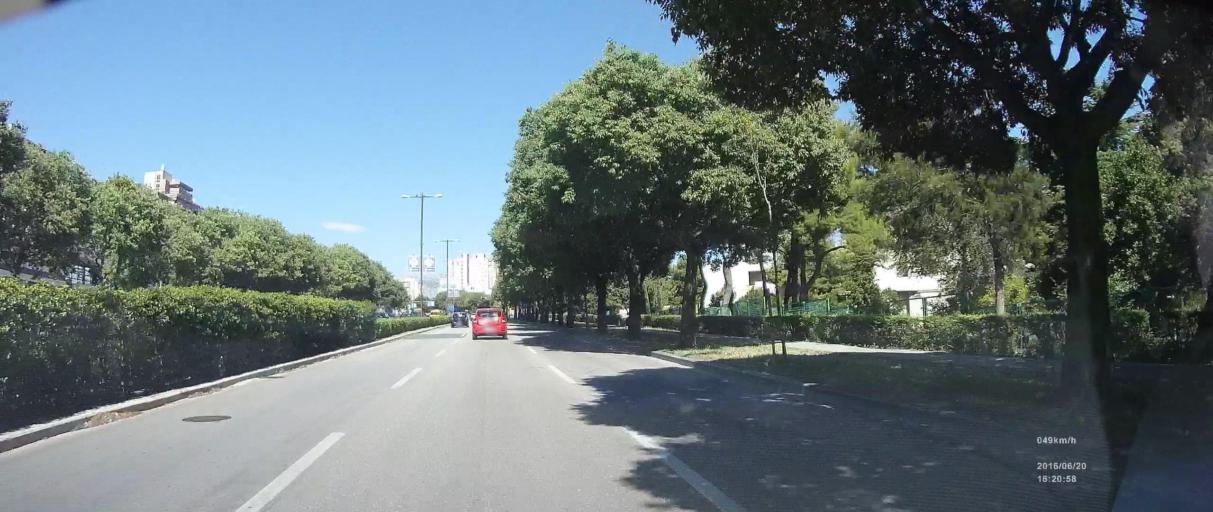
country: HR
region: Splitsko-Dalmatinska
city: Vranjic
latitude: 43.5072
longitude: 16.4685
